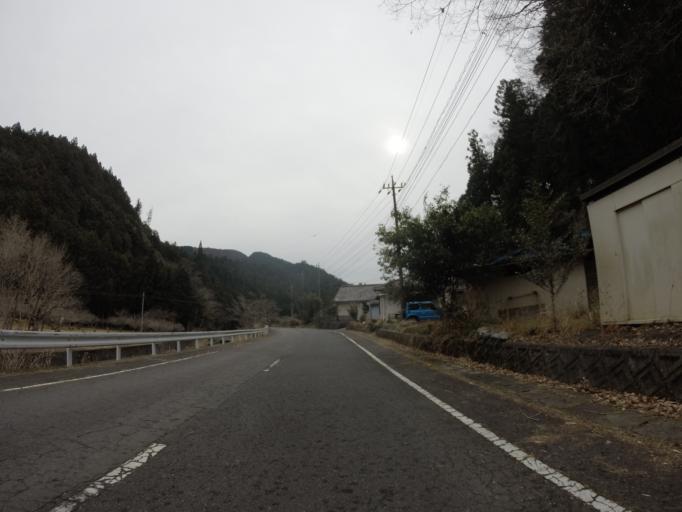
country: JP
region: Shizuoka
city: Fujinomiya
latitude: 35.2727
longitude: 138.5293
